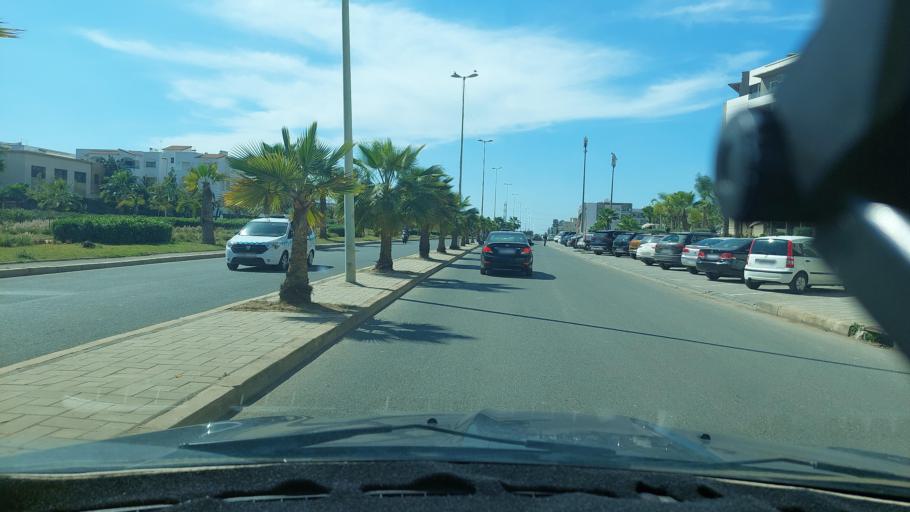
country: MA
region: Grand Casablanca
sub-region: Casablanca
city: Casablanca
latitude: 33.5269
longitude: -7.6113
